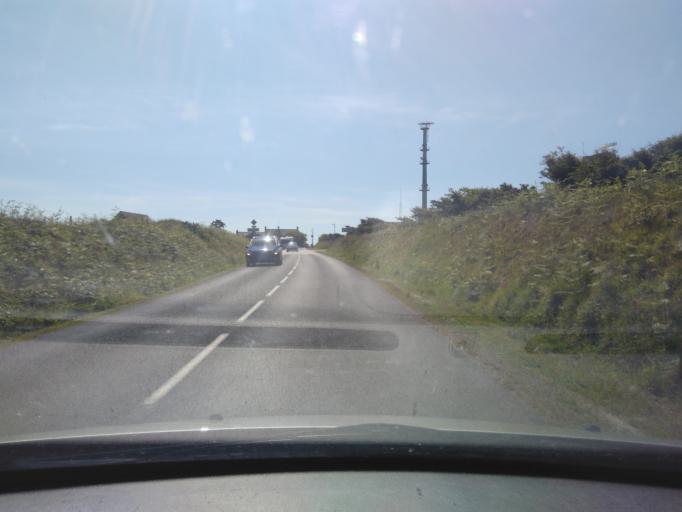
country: FR
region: Lower Normandy
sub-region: Departement de la Manche
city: Beaumont-Hague
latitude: 49.6855
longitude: -1.9086
